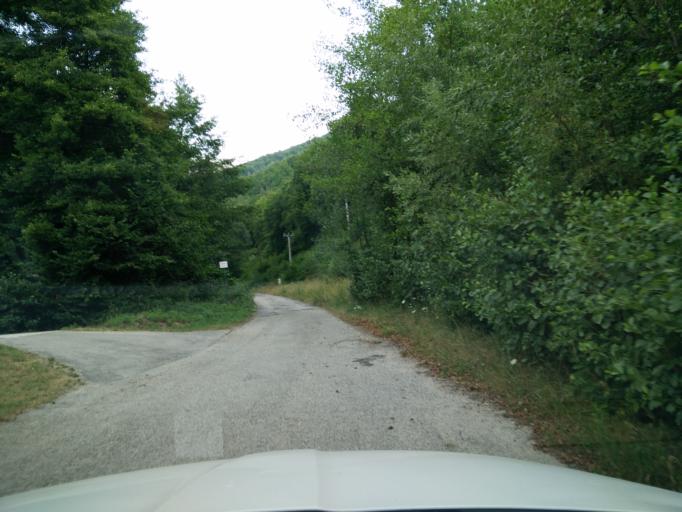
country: SK
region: Nitriansky
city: Novaky
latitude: 48.8120
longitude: 18.4530
